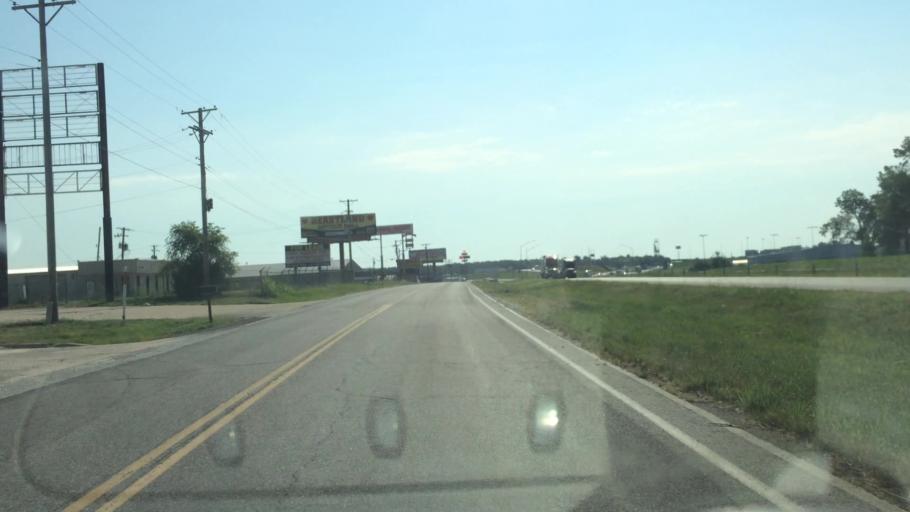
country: US
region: Missouri
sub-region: Greene County
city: Strafford
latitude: 37.2726
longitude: -93.1217
